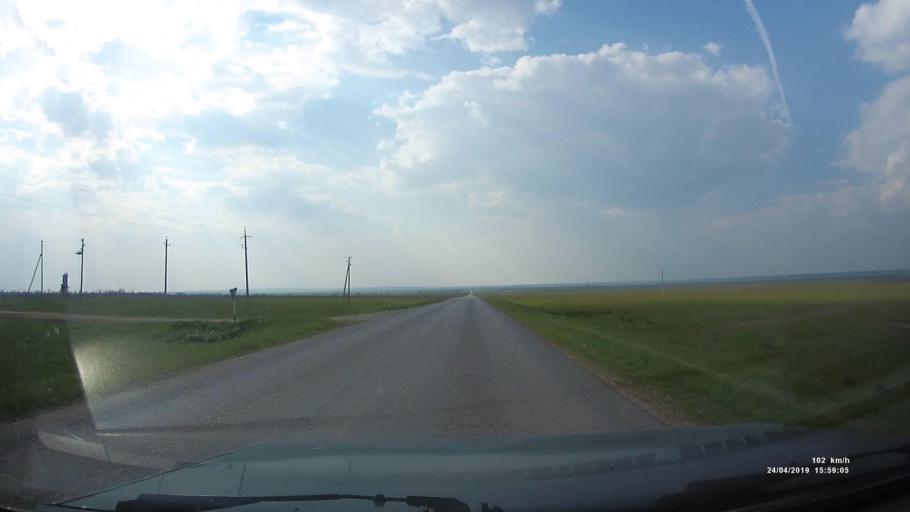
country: RU
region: Kalmykiya
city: Yashalta
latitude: 46.6201
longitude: 42.4785
